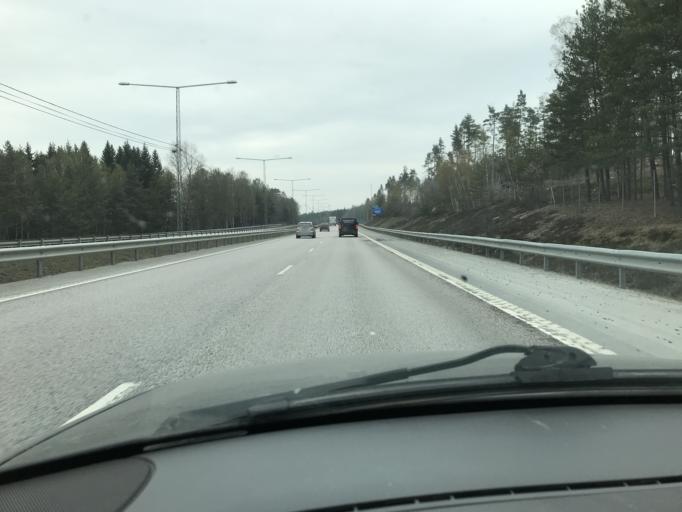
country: SE
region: Stockholm
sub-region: Vallentuna Kommun
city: Vallentuna
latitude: 59.4827
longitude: 18.1647
